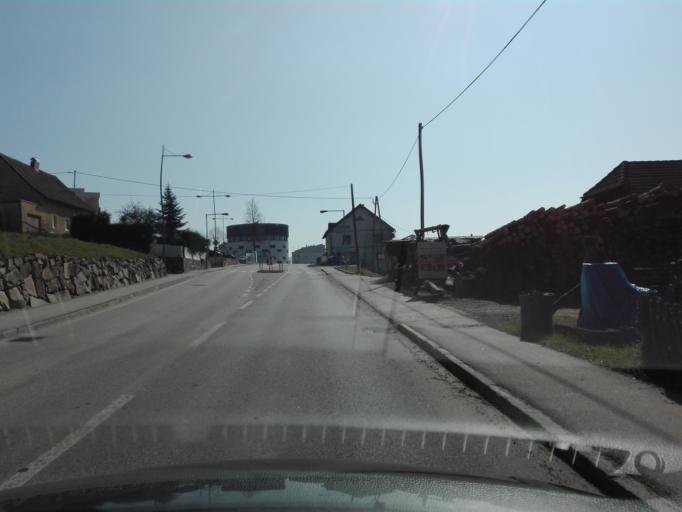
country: AT
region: Upper Austria
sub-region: Politischer Bezirk Urfahr-Umgebung
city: Engerwitzdorf
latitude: 48.3674
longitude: 14.4711
